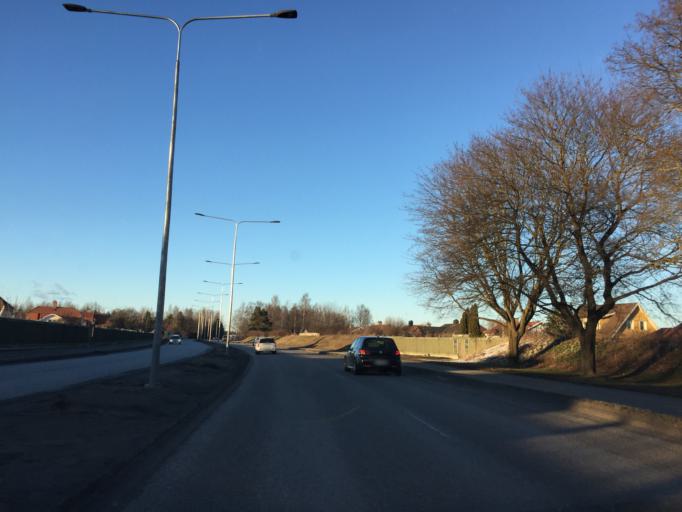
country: SE
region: OErebro
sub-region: Orebro Kommun
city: Orebro
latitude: 59.2907
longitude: 15.2250
